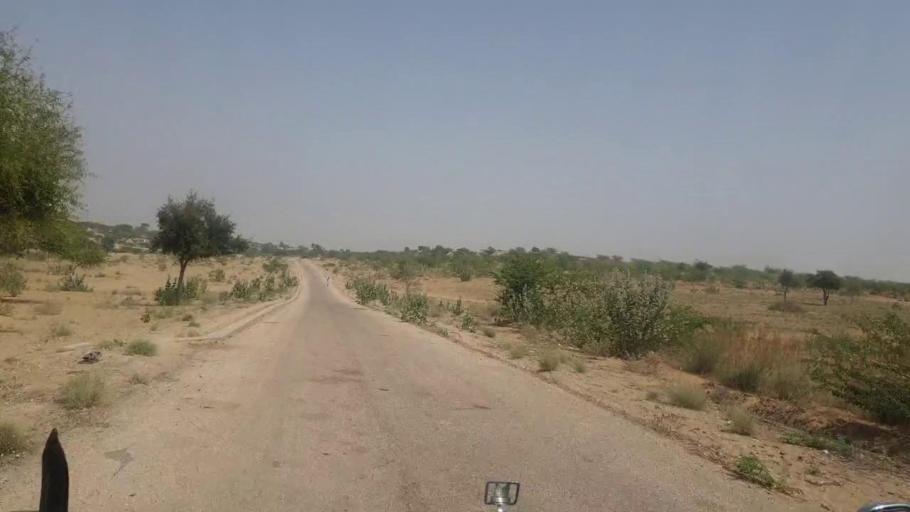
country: PK
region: Sindh
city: Umarkot
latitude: 25.2244
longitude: 70.2423
